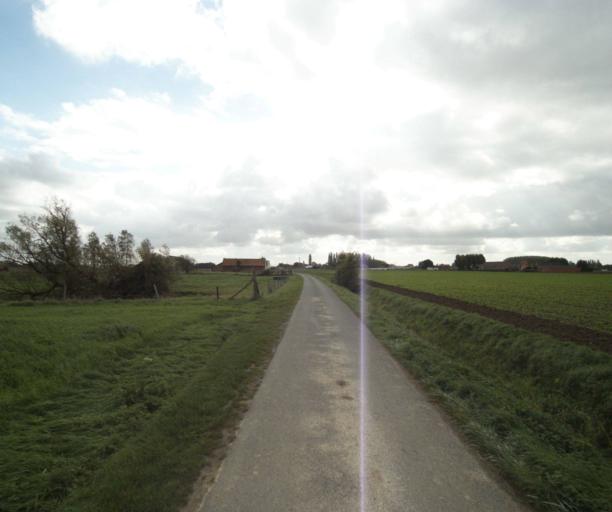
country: FR
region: Nord-Pas-de-Calais
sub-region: Departement du Nord
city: Frelinghien
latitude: 50.7112
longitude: 2.9538
